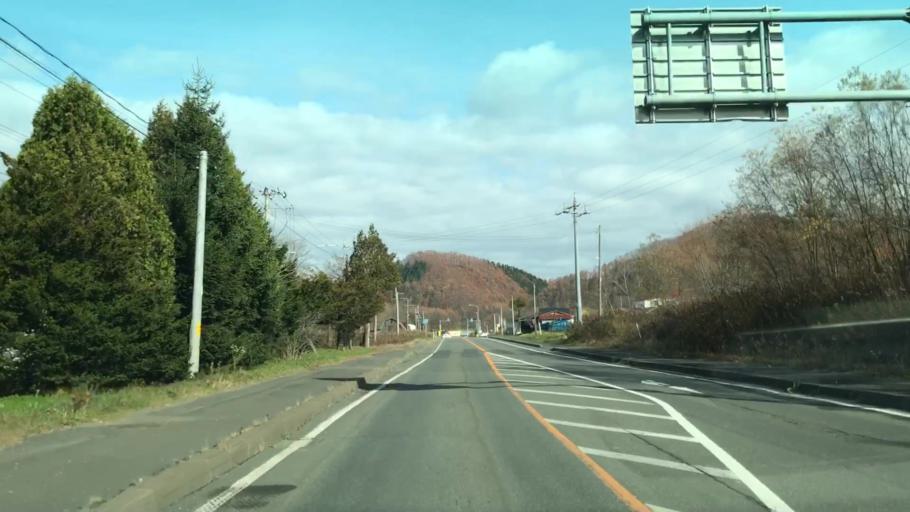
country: JP
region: Hokkaido
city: Shizunai-furukawacho
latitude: 42.5961
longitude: 142.1461
